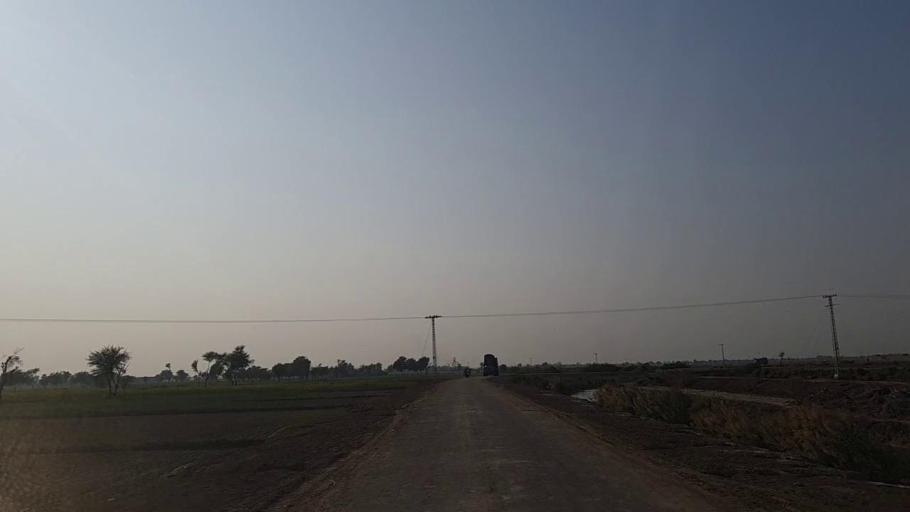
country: PK
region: Sindh
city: Jam Sahib
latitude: 26.2856
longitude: 68.6123
